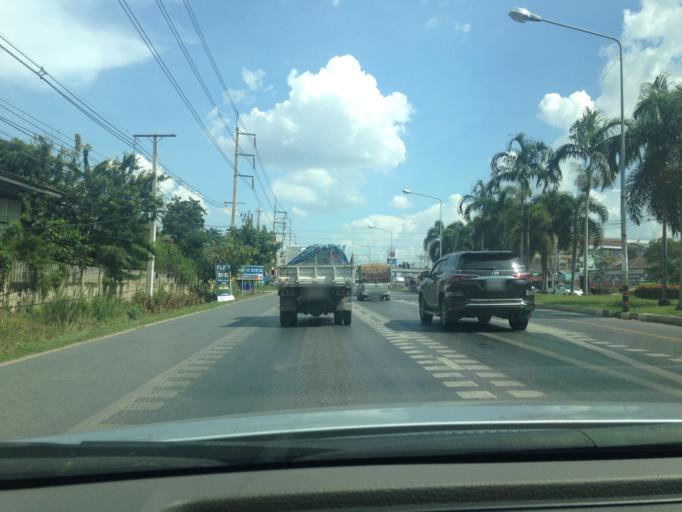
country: TH
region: Phra Nakhon Si Ayutthaya
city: Ban Bang Kadi Pathum Thani
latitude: 13.9922
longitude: 100.5803
